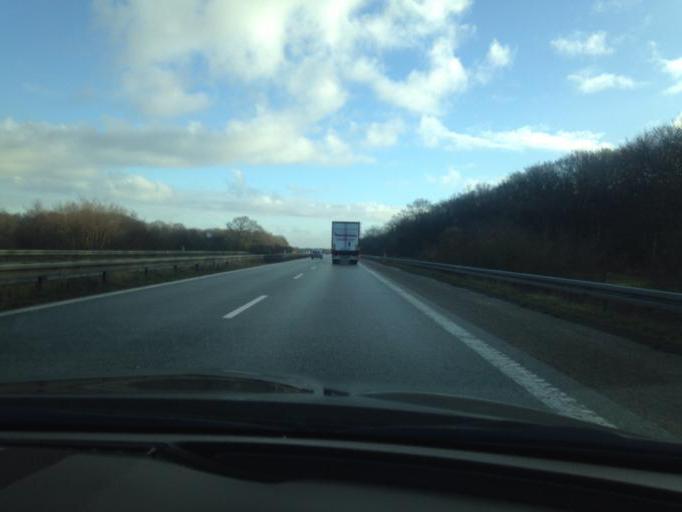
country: DK
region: South Denmark
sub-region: Vejen Kommune
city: Vejen
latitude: 55.4982
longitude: 9.0806
